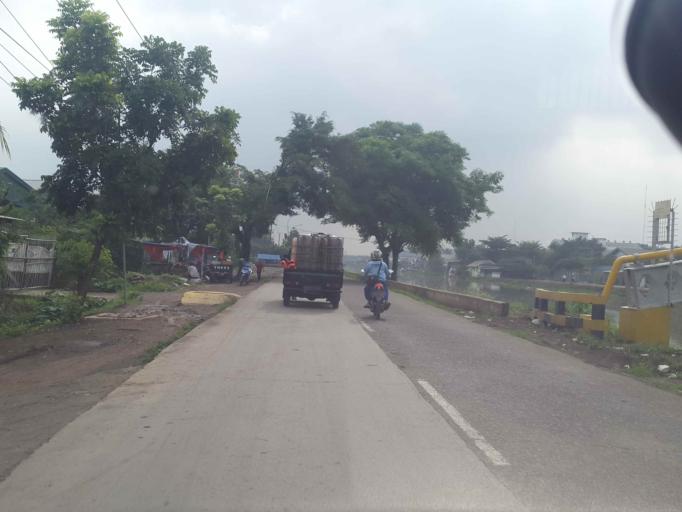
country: ID
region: West Java
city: Cikarang
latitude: -6.2833
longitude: 107.1035
